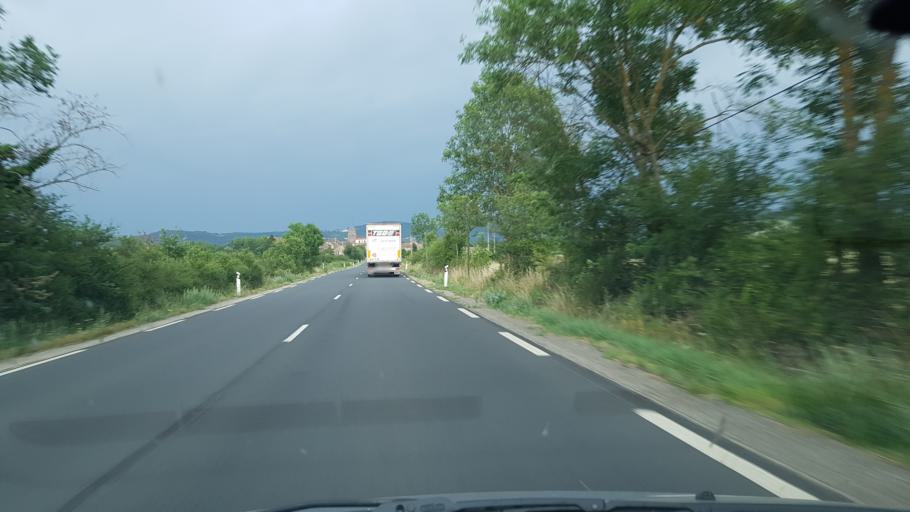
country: FR
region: Auvergne
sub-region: Departement de la Haute-Loire
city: Paulhaguet
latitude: 45.1614
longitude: 3.5352
